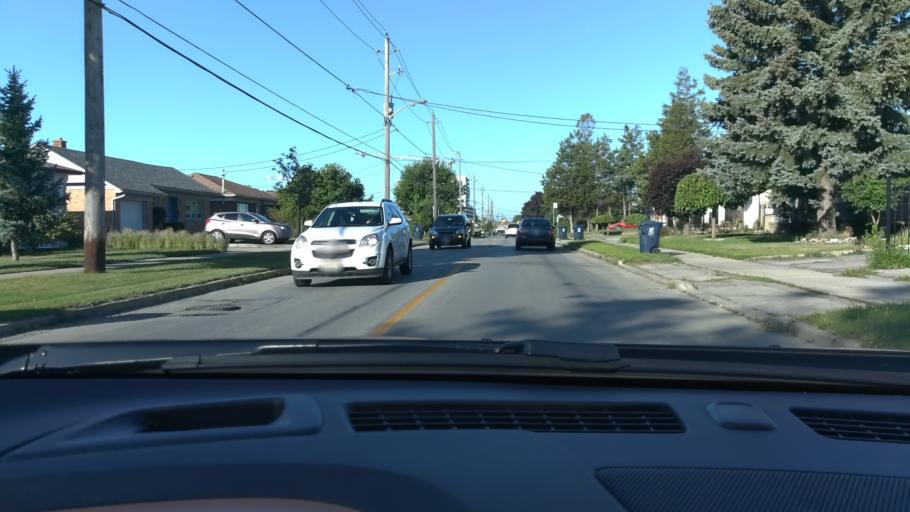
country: CA
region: Ontario
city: Toronto
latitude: 43.7248
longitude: -79.4414
